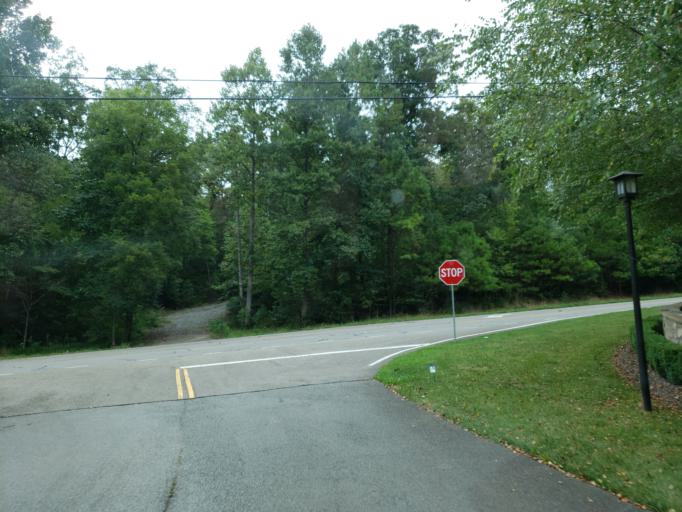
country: US
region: Georgia
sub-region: Gilmer County
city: Ellijay
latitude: 34.6392
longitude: -84.5703
